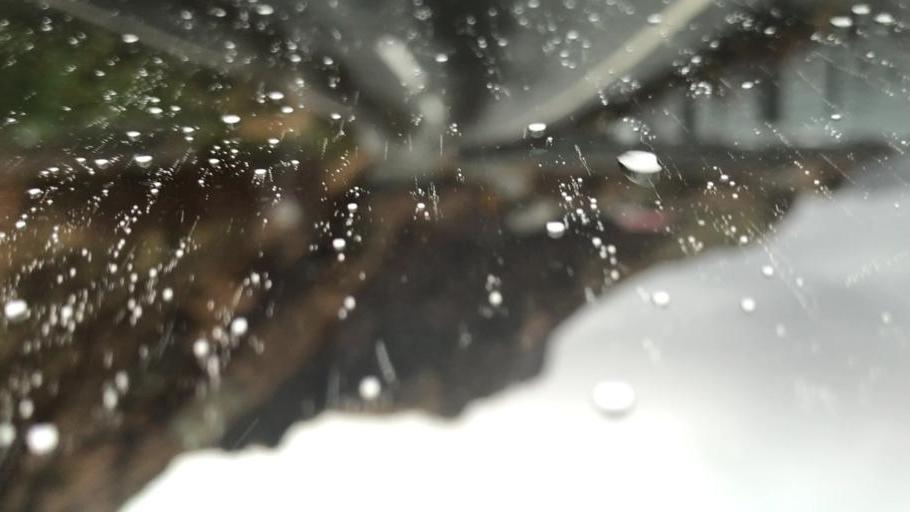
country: JP
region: Hokkaido
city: Iwanai
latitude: 43.3006
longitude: 140.3546
